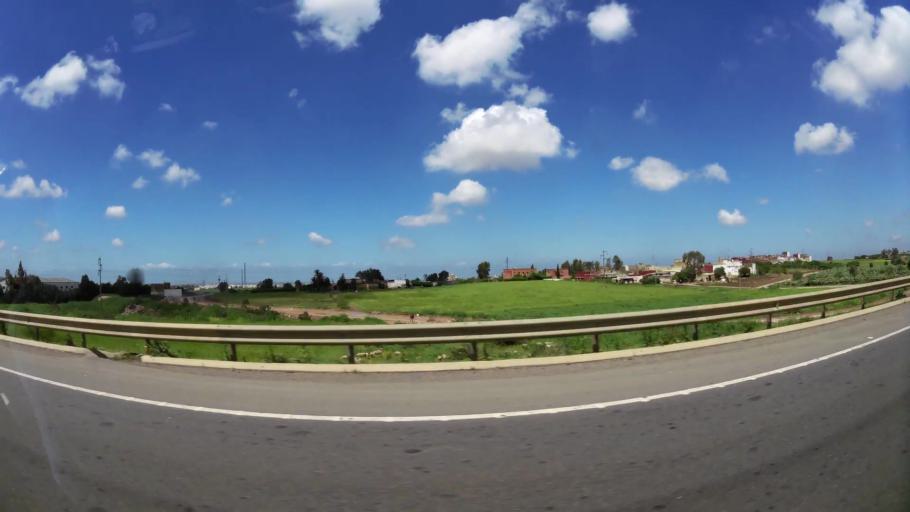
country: MA
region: Grand Casablanca
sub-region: Casablanca
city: Casablanca
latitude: 33.5148
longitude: -7.5948
